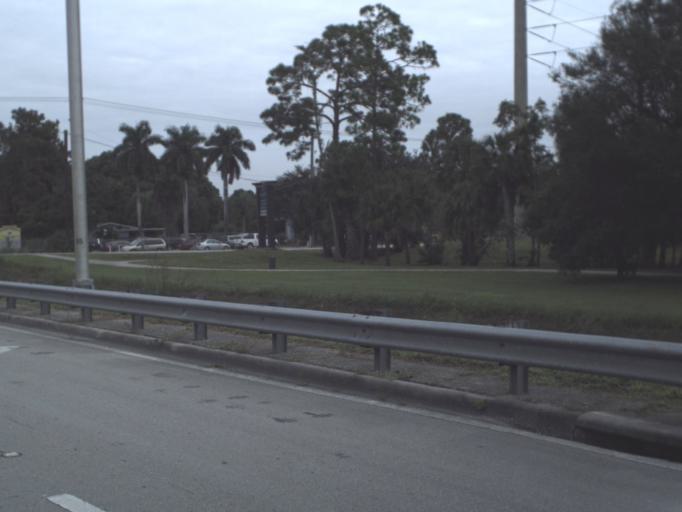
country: US
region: Florida
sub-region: Collier County
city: Lely Resort
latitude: 26.0945
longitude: -81.6872
